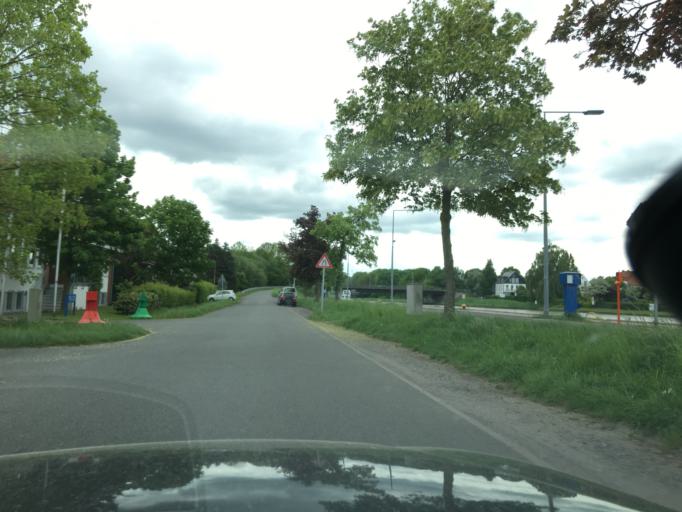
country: DE
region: North Rhine-Westphalia
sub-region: Regierungsbezirk Munster
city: Muenster
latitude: 51.9707
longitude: 7.6643
